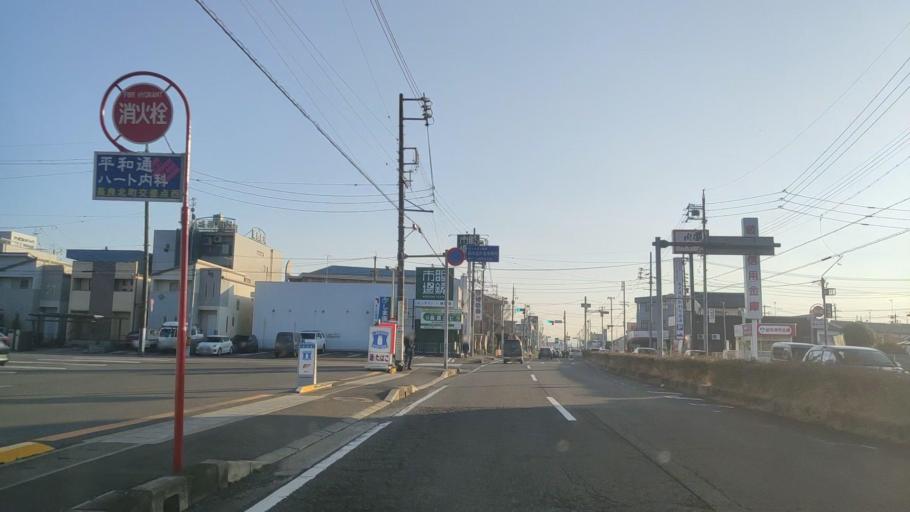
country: JP
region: Gifu
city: Gifu-shi
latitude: 35.4374
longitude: 136.7376
